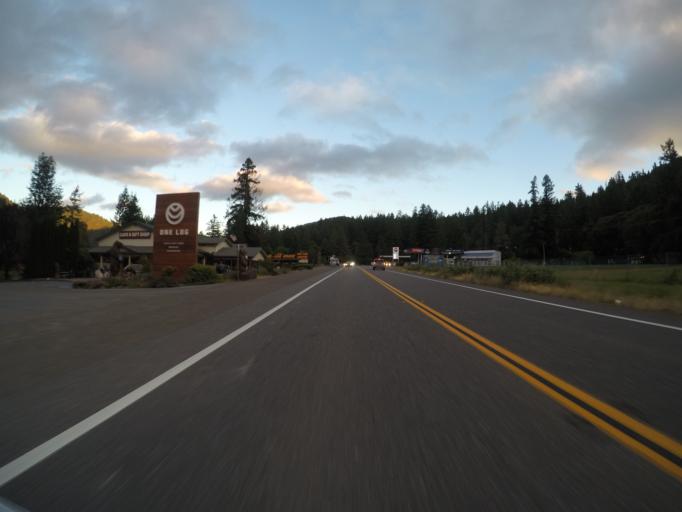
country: US
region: California
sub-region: Humboldt County
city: Redway
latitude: 40.0104
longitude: -123.7906
